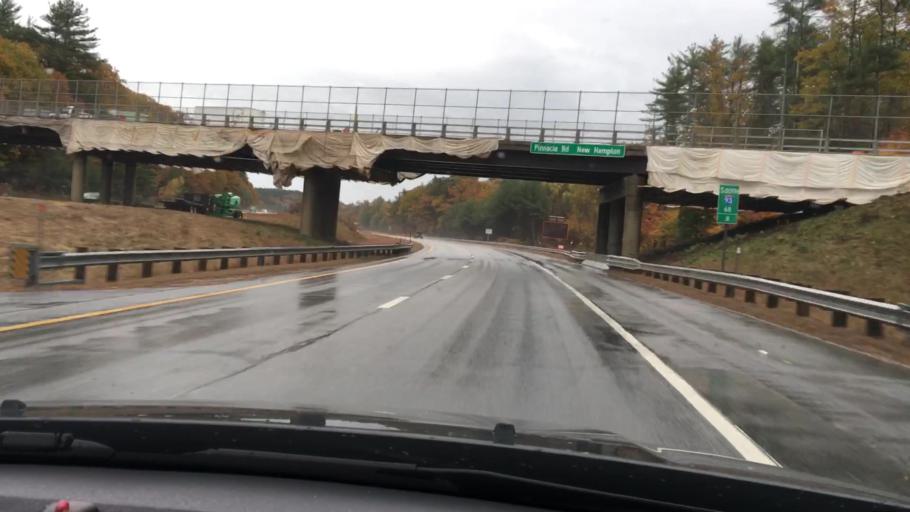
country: US
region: New Hampshire
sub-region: Grafton County
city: Ashland
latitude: 43.6078
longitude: -71.6399
